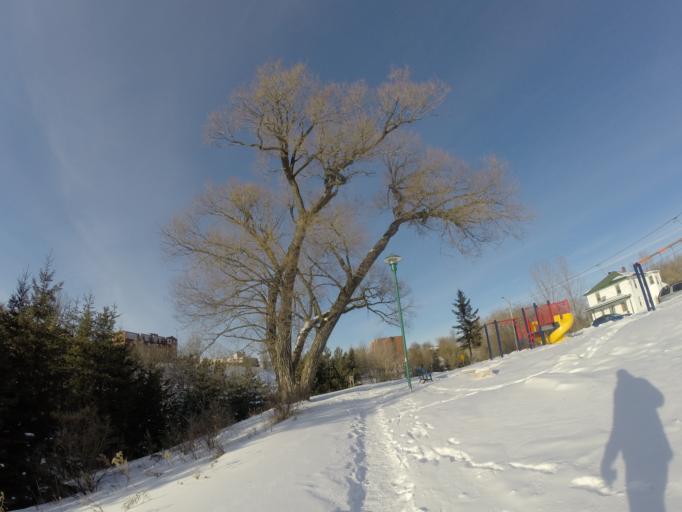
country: CA
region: Ontario
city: Greater Sudbury
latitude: 46.4967
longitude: -80.9871
